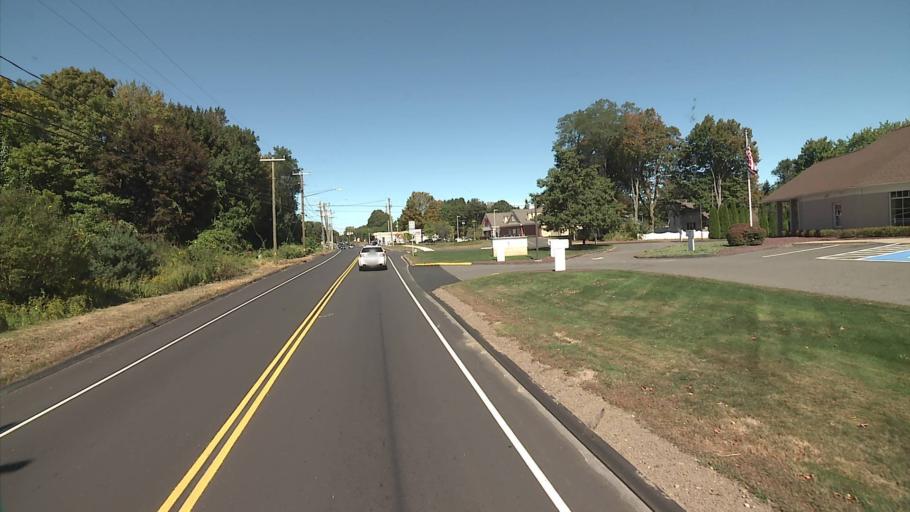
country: US
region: Connecticut
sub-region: New Haven County
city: Prospect
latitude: 41.5063
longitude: -72.9803
